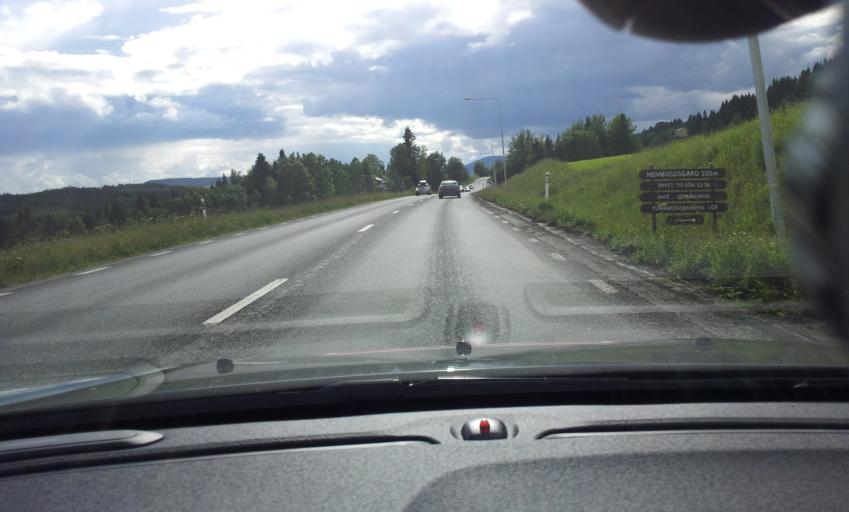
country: SE
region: Jaemtland
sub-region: Are Kommun
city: Jarpen
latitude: 63.3307
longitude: 13.4063
